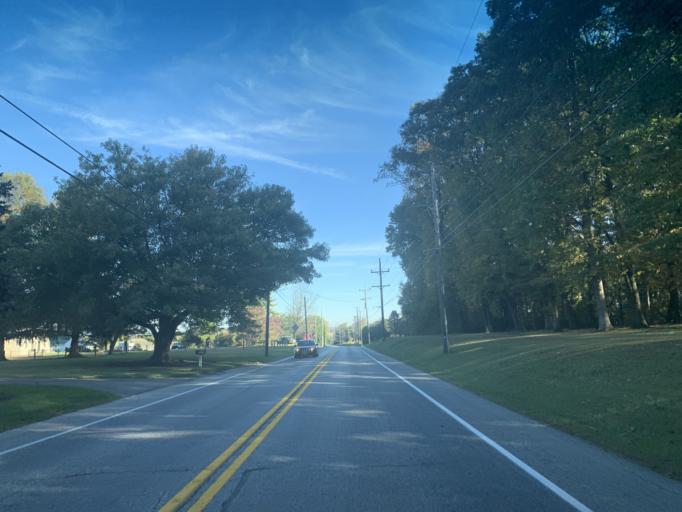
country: US
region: Pennsylvania
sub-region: Chester County
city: Parkesburg
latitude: 39.8716
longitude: -75.9230
